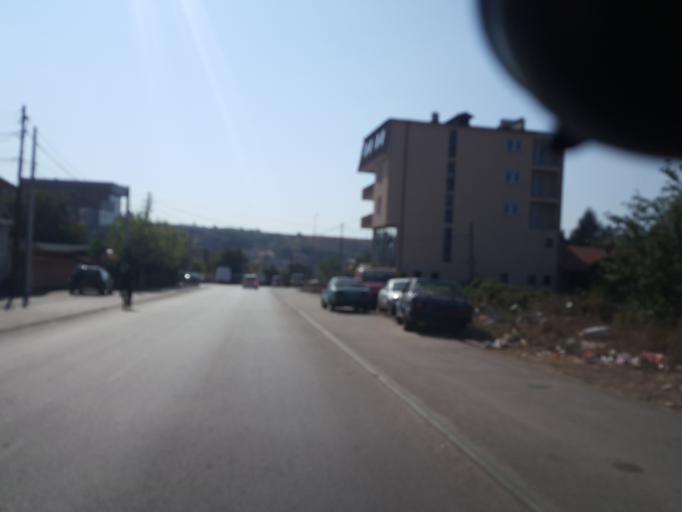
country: XK
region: Gjakova
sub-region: Komuna e Gjakoves
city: Gjakove
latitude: 42.3928
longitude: 20.4251
